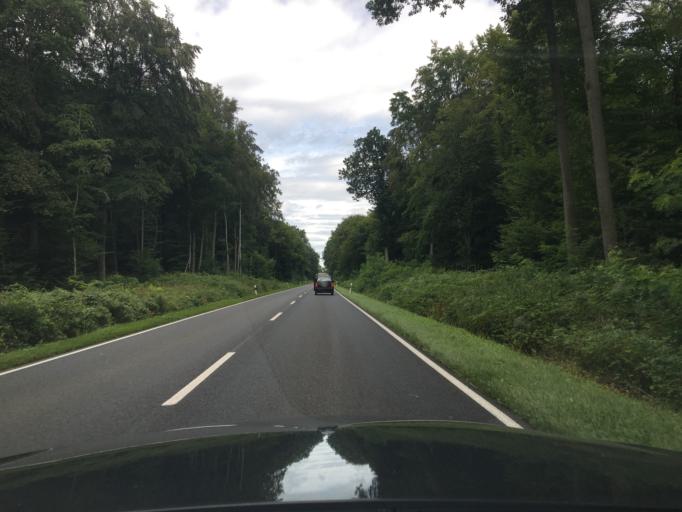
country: DE
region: Brandenburg
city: Gransee
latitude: 53.0649
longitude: 13.1853
